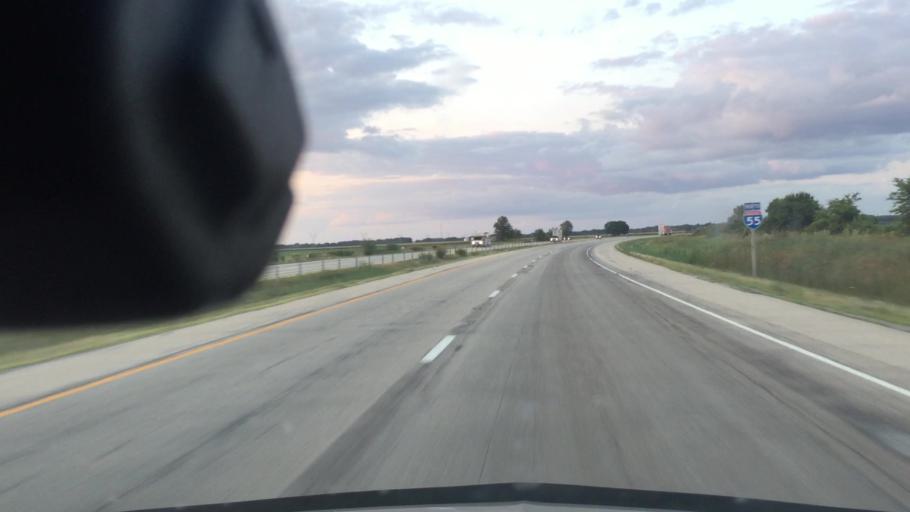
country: US
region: Illinois
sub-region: Grundy County
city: Gardner
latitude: 41.1917
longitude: -88.3193
